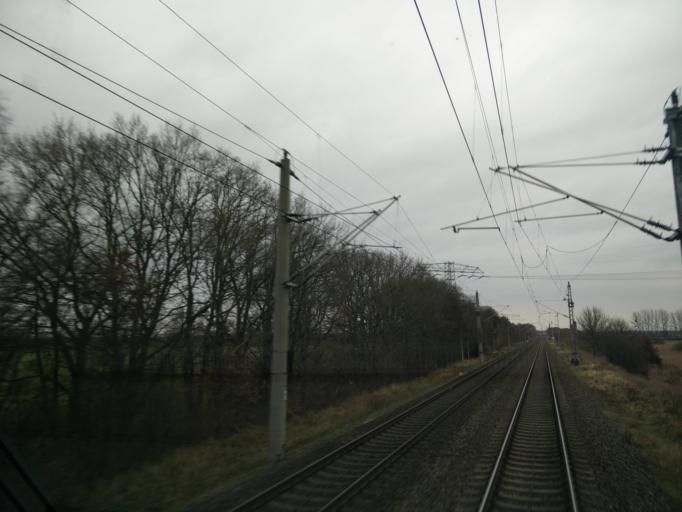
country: DE
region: Brandenburg
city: Breese
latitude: 52.9914
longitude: 11.8121
